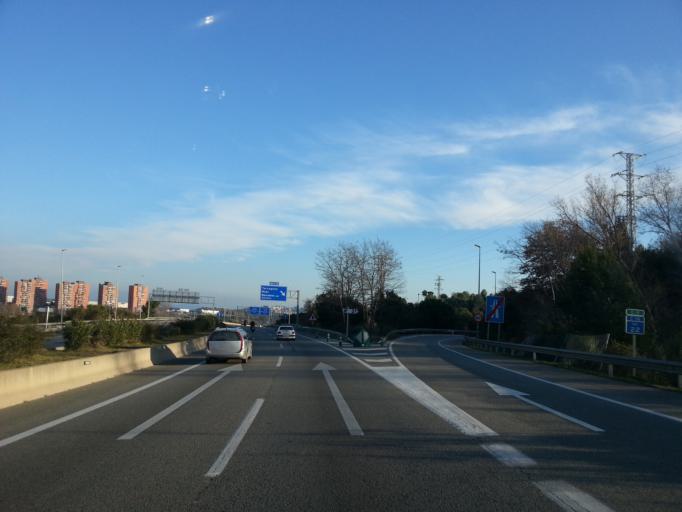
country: ES
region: Catalonia
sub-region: Provincia de Barcelona
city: Terrassa
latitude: 41.5489
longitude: 2.0075
